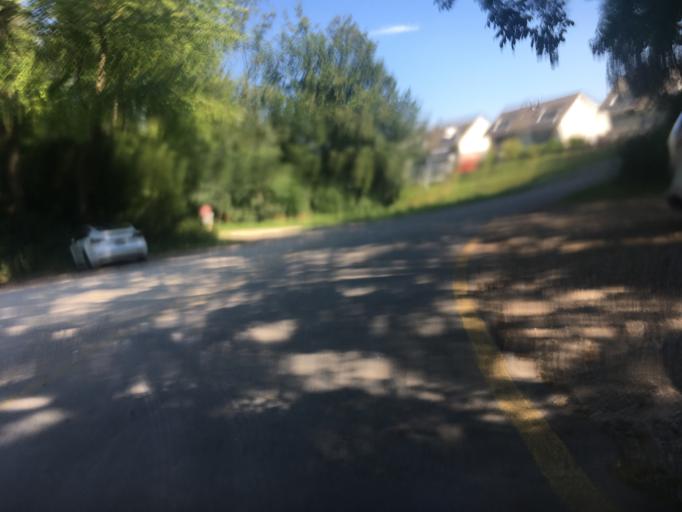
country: CH
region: Bern
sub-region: Emmental District
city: Kirchberg
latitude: 47.0777
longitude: 7.5897
